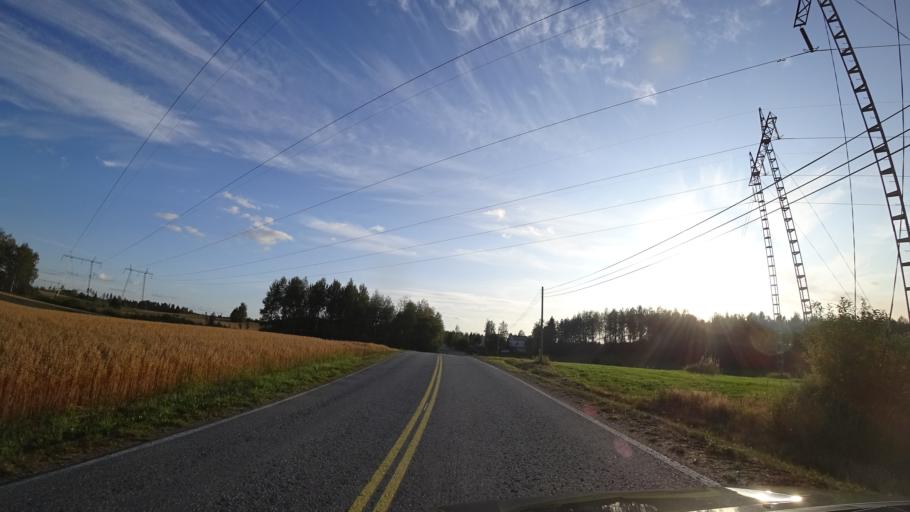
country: FI
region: Haeme
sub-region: Haemeenlinna
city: Lammi
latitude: 61.0366
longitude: 24.9275
